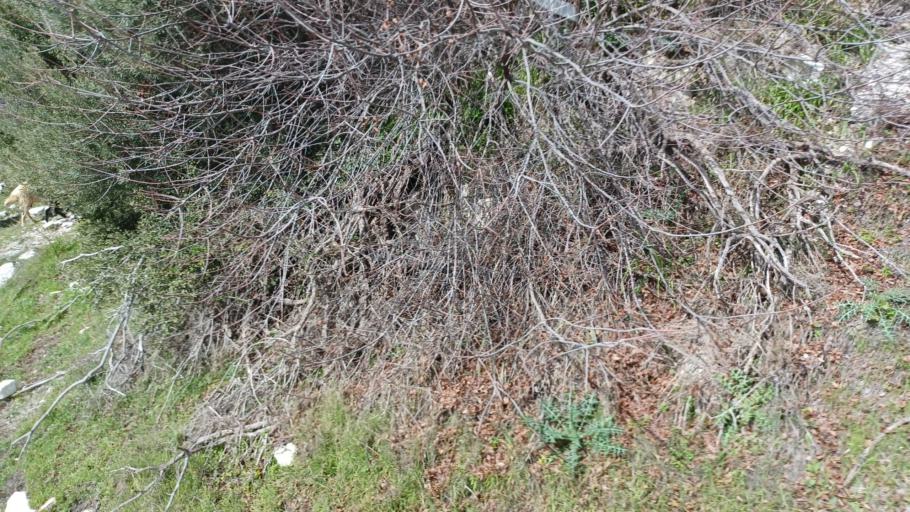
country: CY
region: Limassol
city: Pachna
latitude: 34.7987
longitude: 32.6940
